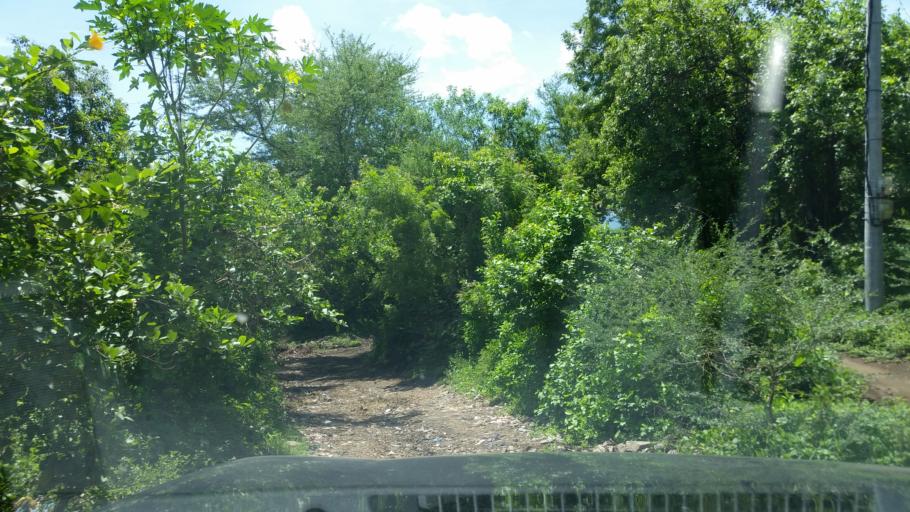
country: NI
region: Chinandega
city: Puerto Morazan
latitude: 12.7629
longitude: -87.1225
